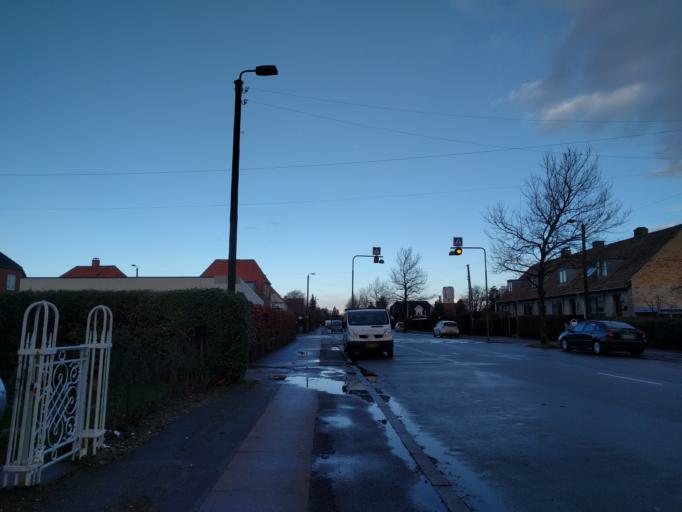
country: DK
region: Capital Region
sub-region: Tarnby Kommune
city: Tarnby
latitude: 55.6534
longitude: 12.6312
